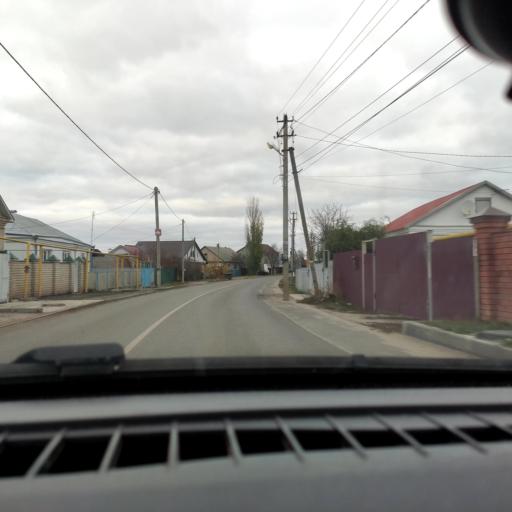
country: RU
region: Voronezj
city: Podgornoye
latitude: 51.7292
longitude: 39.1379
